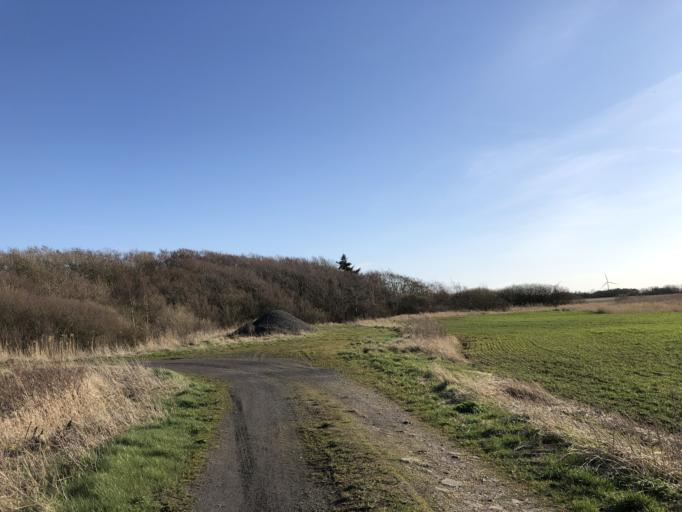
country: DK
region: Central Jutland
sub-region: Holstebro Kommune
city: Ulfborg
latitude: 56.3285
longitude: 8.3275
